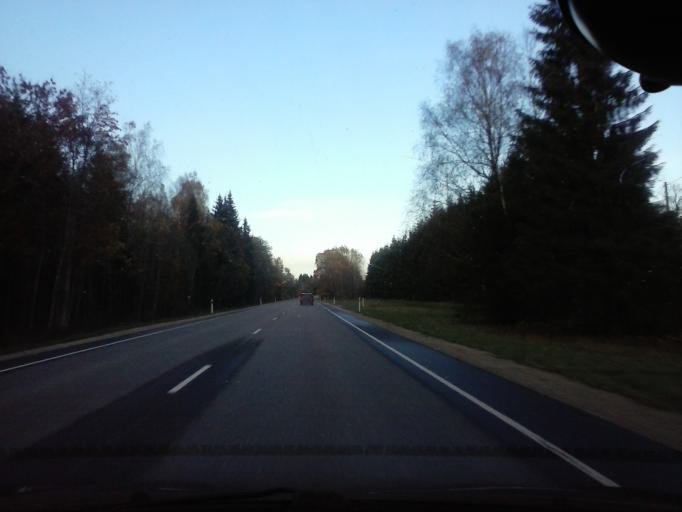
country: EE
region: Harju
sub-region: Nissi vald
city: Turba
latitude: 58.9887
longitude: 24.0179
